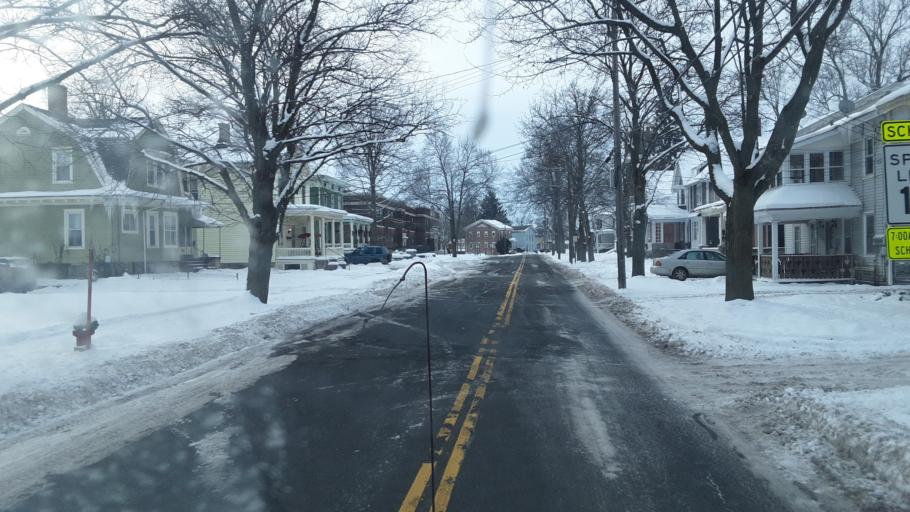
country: US
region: New York
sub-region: Wayne County
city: Lyons
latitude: 43.0673
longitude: -76.9913
